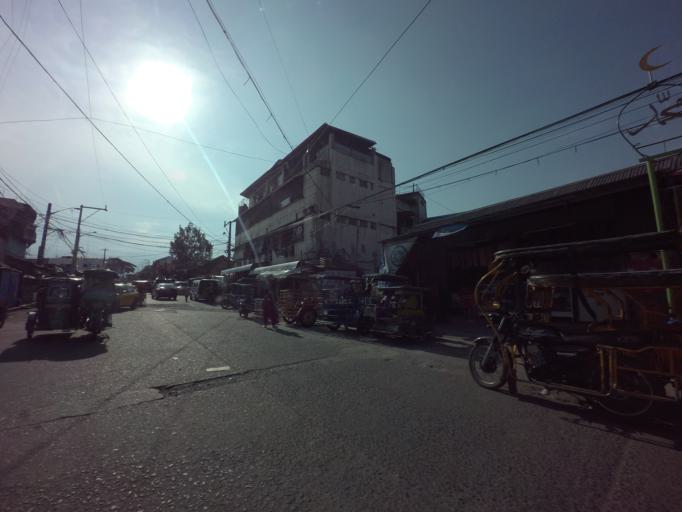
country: PH
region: Calabarzon
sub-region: Province of Rizal
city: Taguig
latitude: 14.4972
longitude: 121.0570
